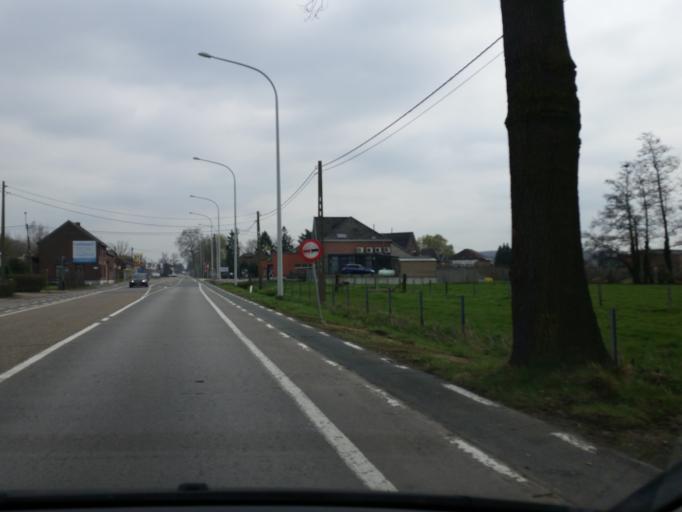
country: BE
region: Flanders
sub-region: Provincie Vlaams-Brabant
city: Herent
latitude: 50.9190
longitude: 4.6502
